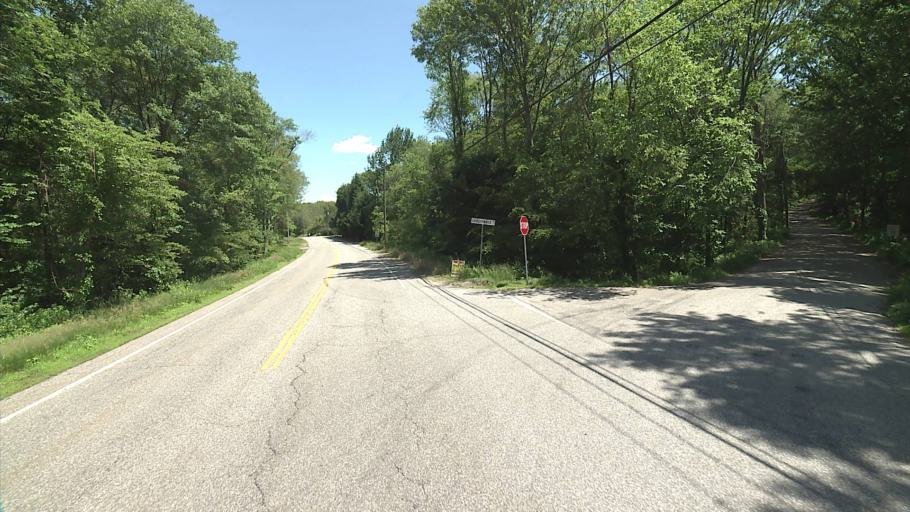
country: US
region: Connecticut
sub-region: New London County
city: Preston City
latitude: 41.5035
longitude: -71.8913
